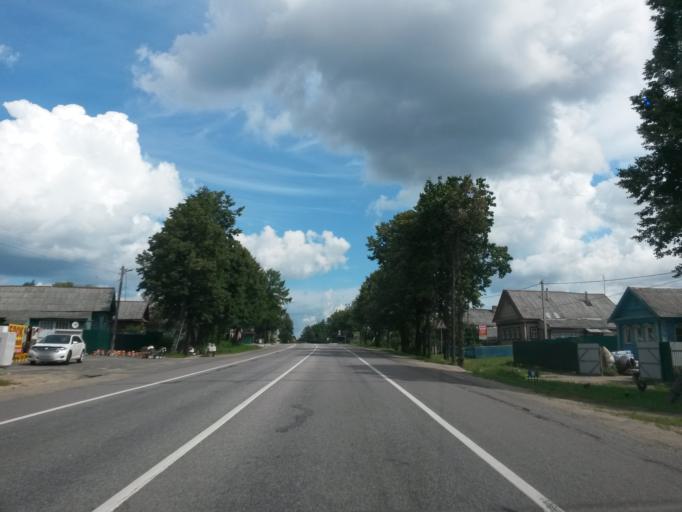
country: RU
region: Jaroslavl
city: Pereslavl'-Zalesskiy
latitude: 56.6863
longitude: 38.7445
